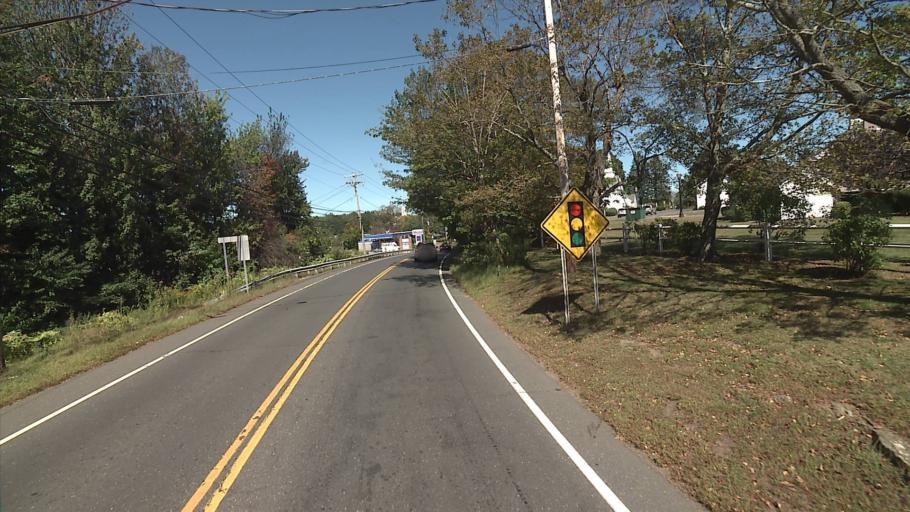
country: US
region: Connecticut
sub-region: New Haven County
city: Prospect
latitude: 41.5008
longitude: -72.9789
